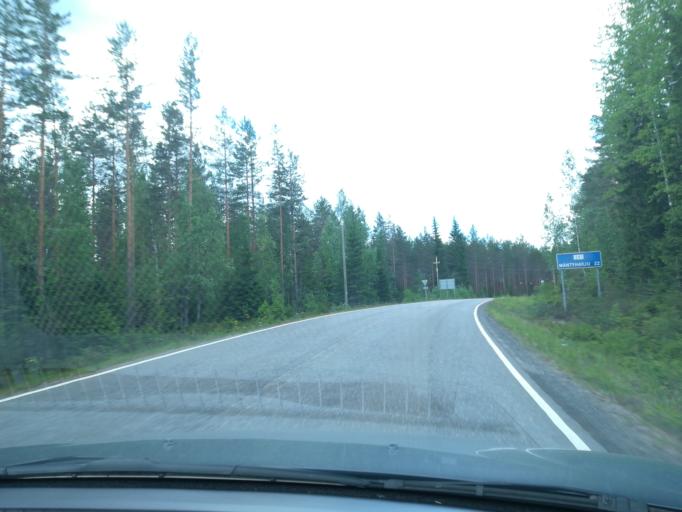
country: FI
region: Southern Savonia
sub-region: Mikkeli
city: Ristiina
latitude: 61.3461
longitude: 27.1825
